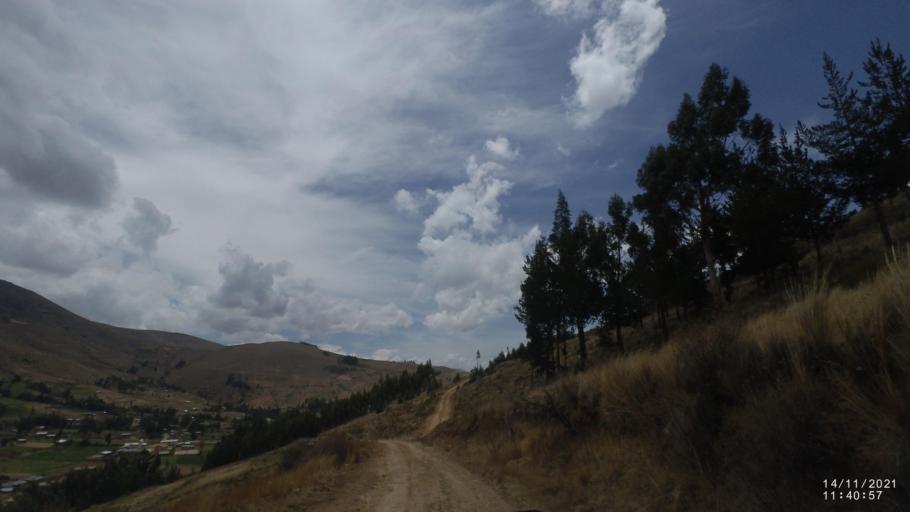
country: BO
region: Cochabamba
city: Colomi
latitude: -17.3524
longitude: -65.9944
